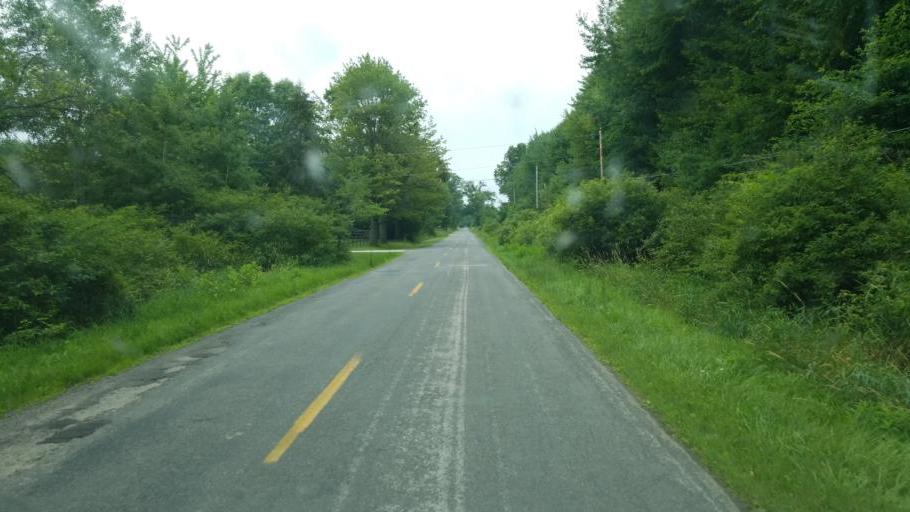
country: US
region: Ohio
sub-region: Trumbull County
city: Cortland
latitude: 41.4120
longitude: -80.7769
